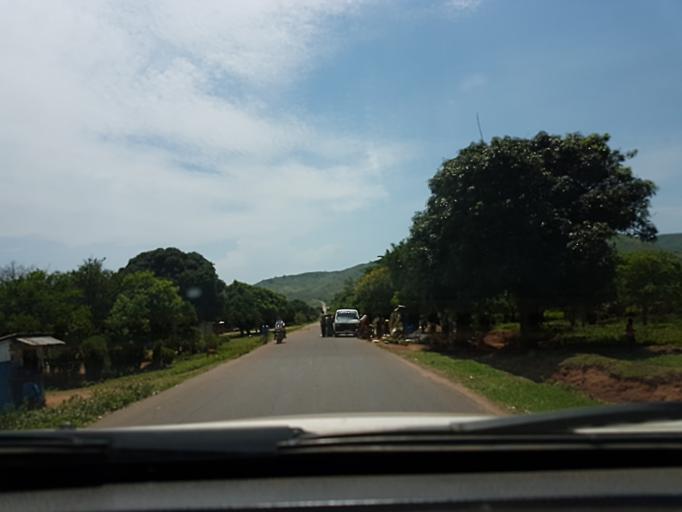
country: BI
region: Cibitoke
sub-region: Commune of Buganda
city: Buganda
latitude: -3.0835
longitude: 29.1256
